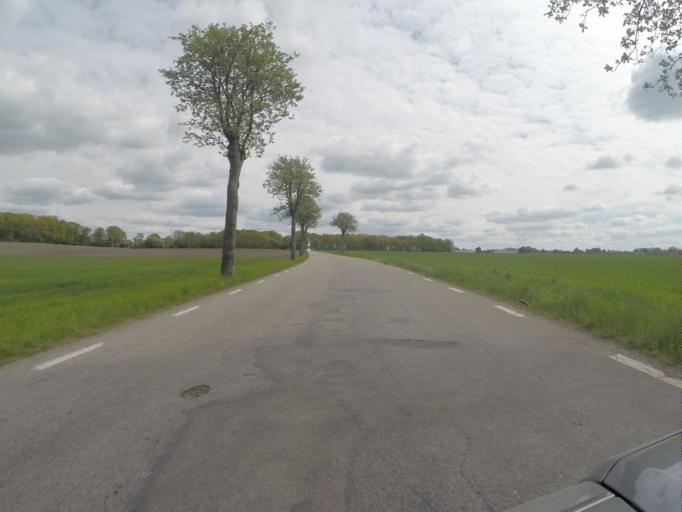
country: SE
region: Skane
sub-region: Helsingborg
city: Morarp
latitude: 56.0673
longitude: 12.8665
